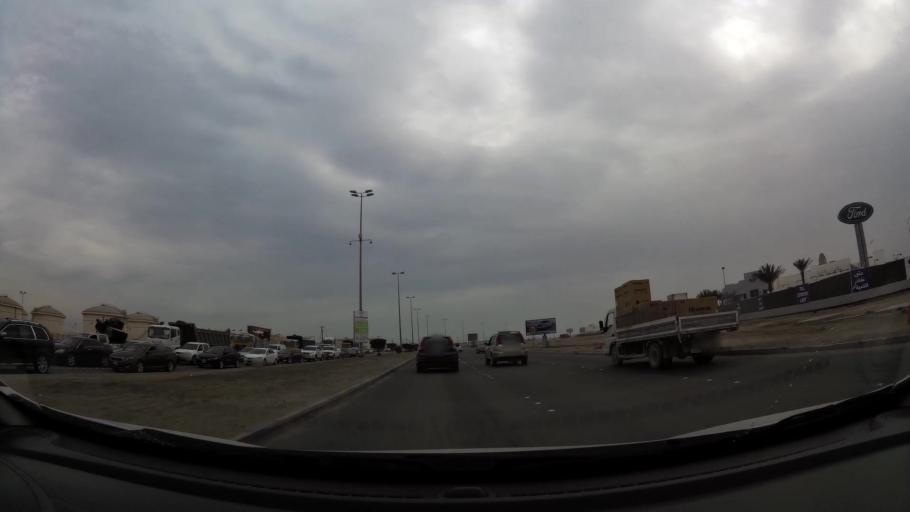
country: BH
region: Northern
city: Sitrah
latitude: 26.1477
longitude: 50.6186
